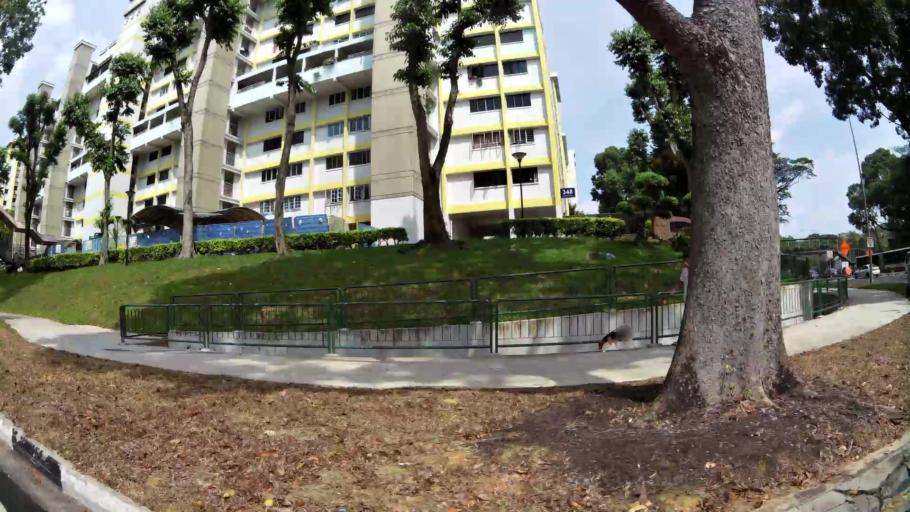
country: SG
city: Singapore
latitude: 1.3166
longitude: 103.7713
